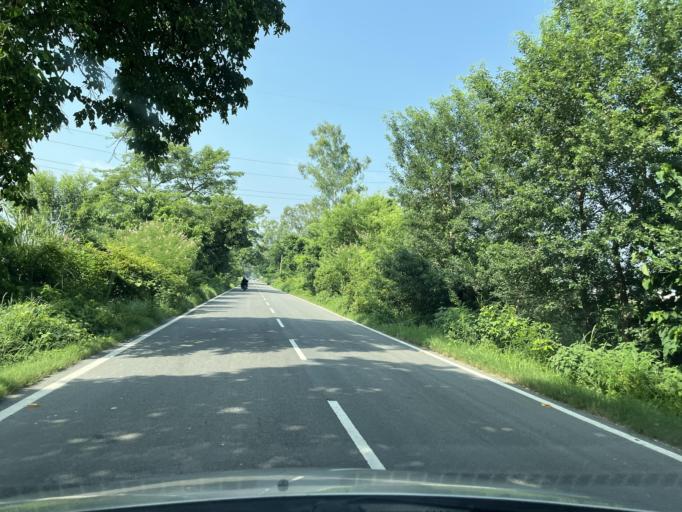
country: IN
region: Uttarakhand
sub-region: Udham Singh Nagar
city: Bazpur
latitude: 29.1944
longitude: 79.1956
